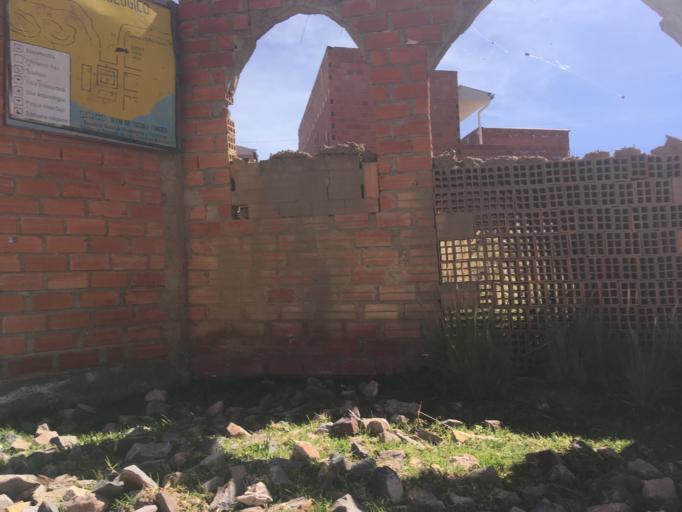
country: BO
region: La Paz
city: San Pedro
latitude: -16.2628
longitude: -68.8805
